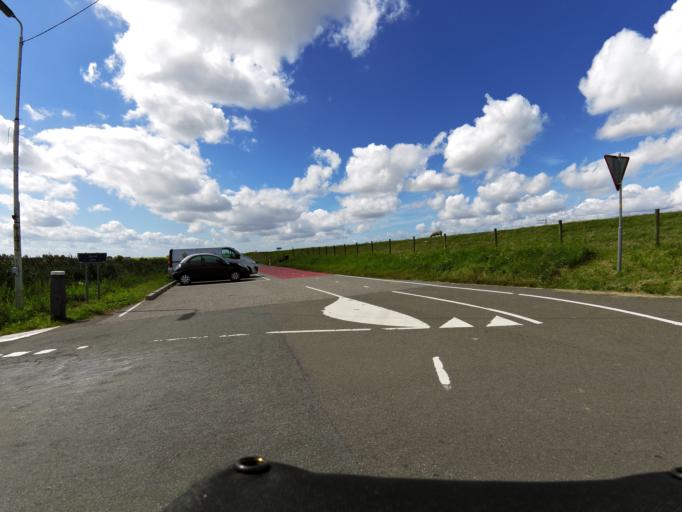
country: NL
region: South Holland
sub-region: Gemeente Spijkenisse
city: Spijkenisse
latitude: 51.8173
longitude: 4.3381
